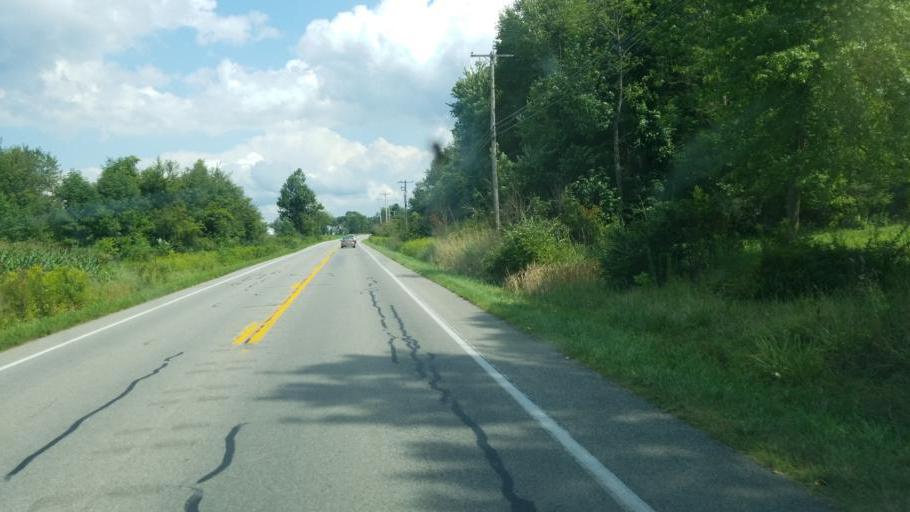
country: US
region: Pennsylvania
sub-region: Crawford County
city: Pymatuning Central
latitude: 41.6059
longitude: -80.4791
